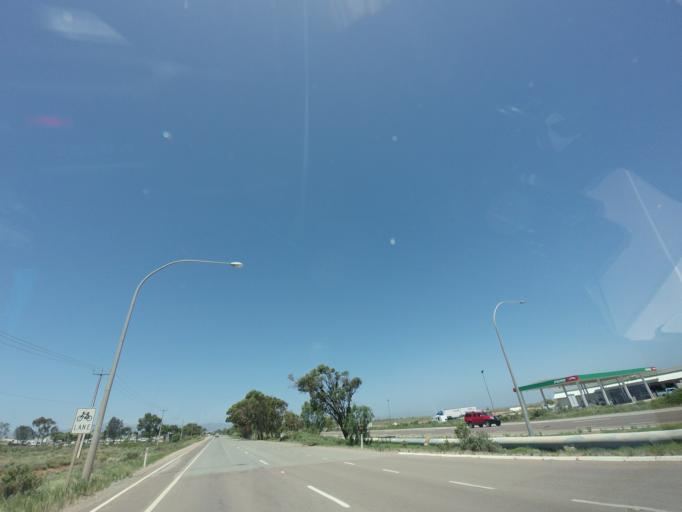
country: AU
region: South Australia
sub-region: Port Augusta
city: Port Augusta
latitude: -32.5111
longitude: 137.8038
